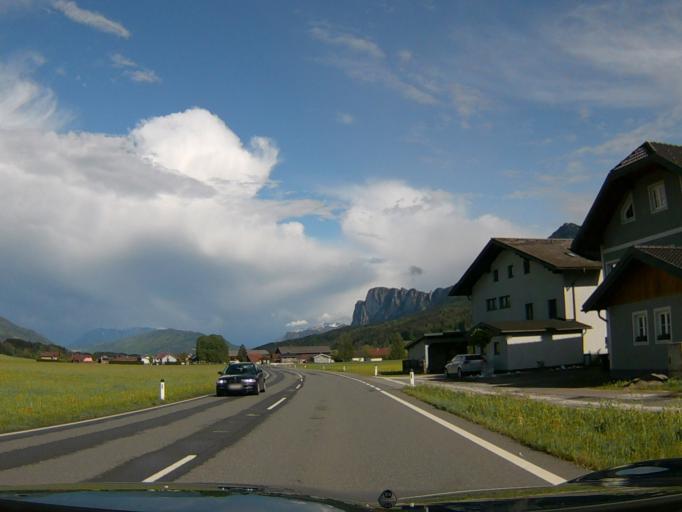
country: AT
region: Salzburg
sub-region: Politischer Bezirk Salzburg-Umgebung
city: Thalgau
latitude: 47.8410
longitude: 13.2706
